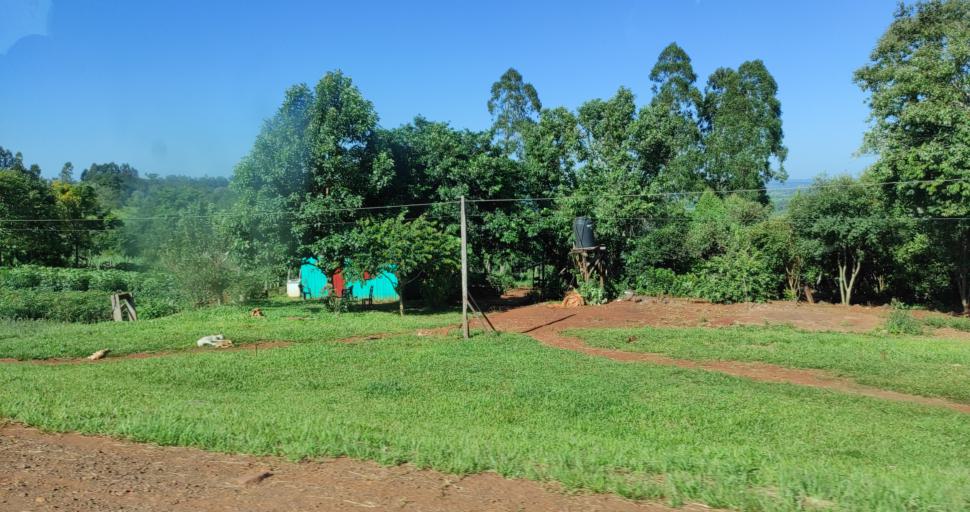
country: AR
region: Misiones
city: El Soberbio
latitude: -27.1849
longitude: -54.1071
